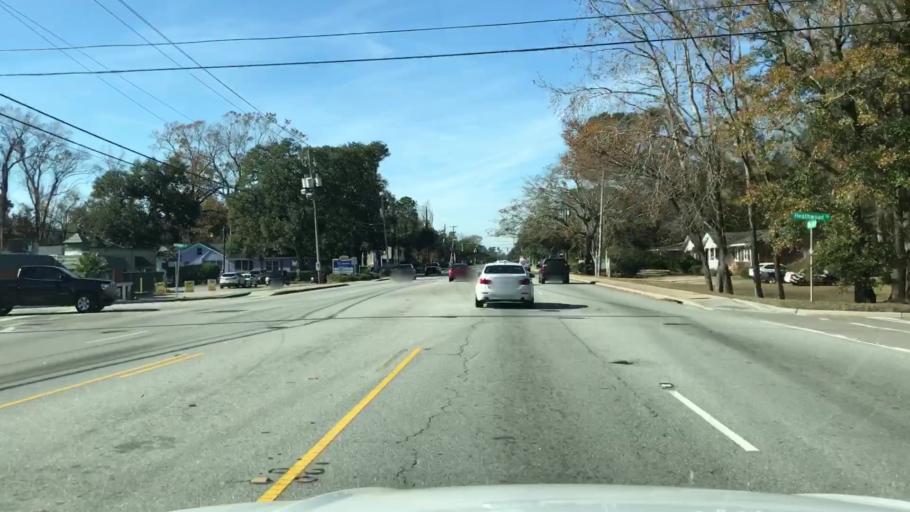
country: US
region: South Carolina
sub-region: Charleston County
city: North Charleston
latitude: 32.7983
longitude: -80.0037
